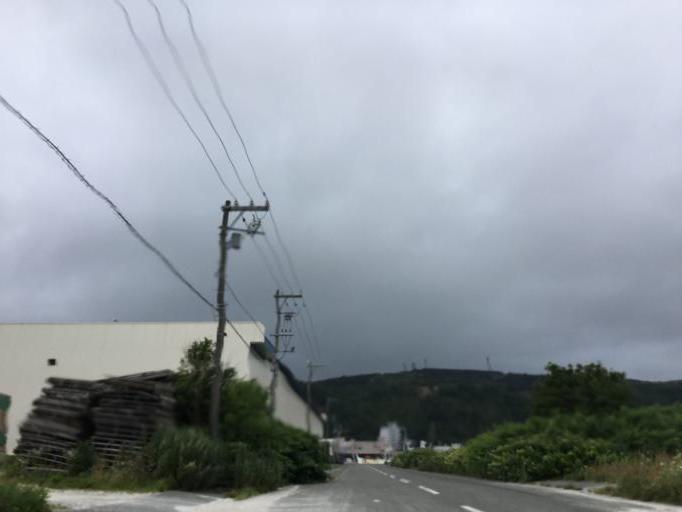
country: JP
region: Hokkaido
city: Wakkanai
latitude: 45.4094
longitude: 141.6817
